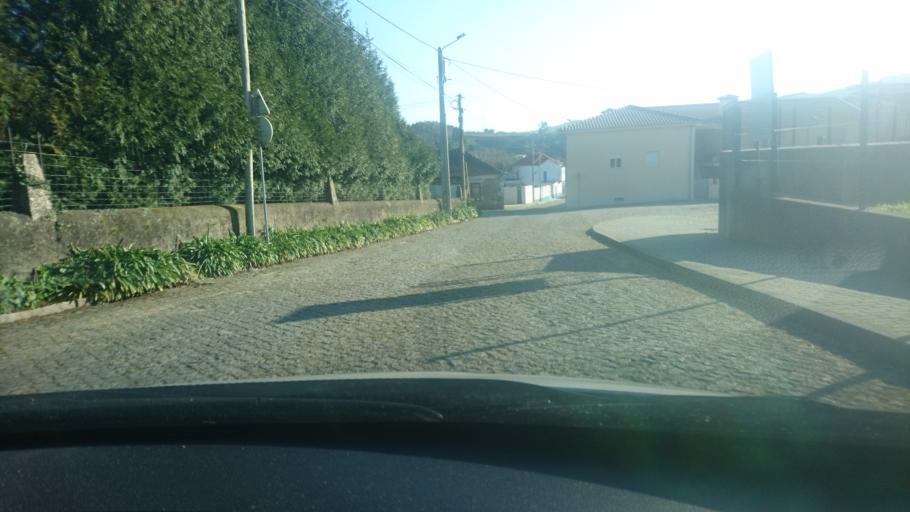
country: PT
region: Porto
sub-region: Paredes
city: Recarei
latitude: 41.1462
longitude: -8.3870
